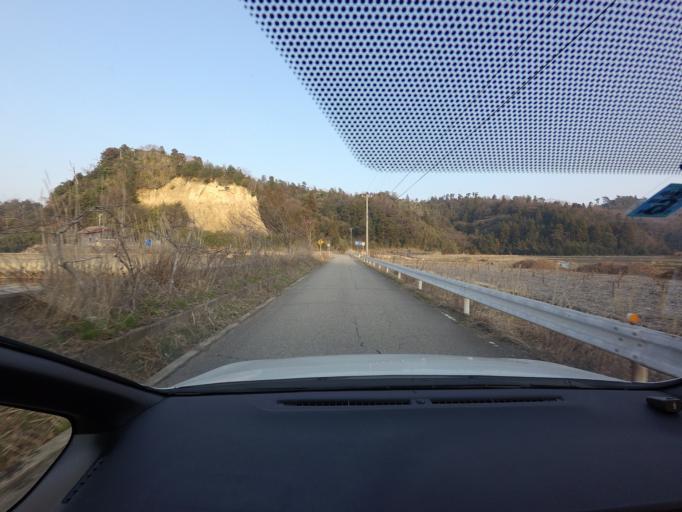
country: JP
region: Ishikawa
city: Nanao
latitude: 37.1424
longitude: 137.0217
